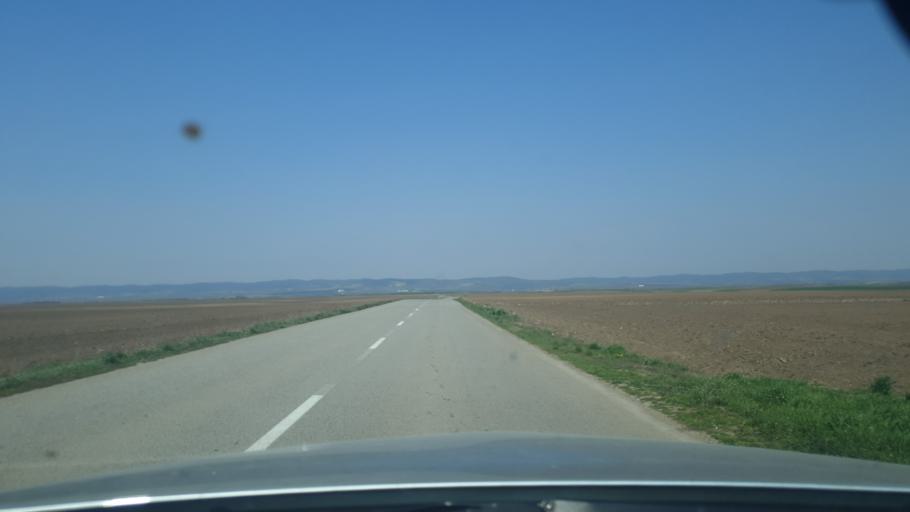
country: RS
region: Autonomna Pokrajina Vojvodina
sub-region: Sremski Okrug
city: Ruma
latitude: 45.0286
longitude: 19.7624
